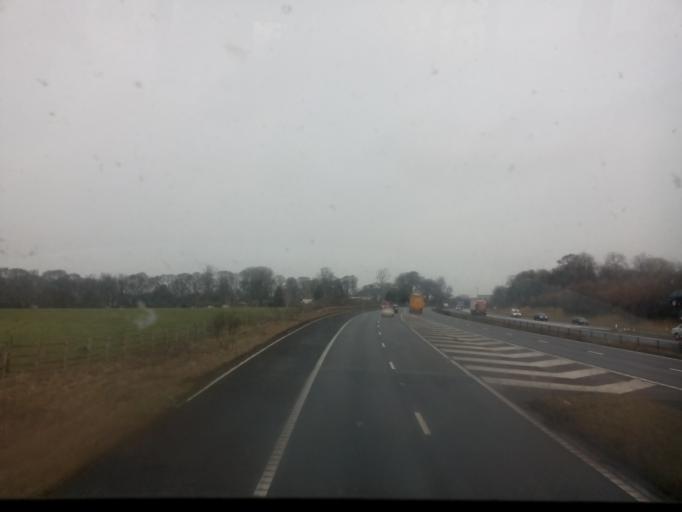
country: GB
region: England
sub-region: County Durham
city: Chester-le-Street
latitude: 54.8697
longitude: -1.5677
